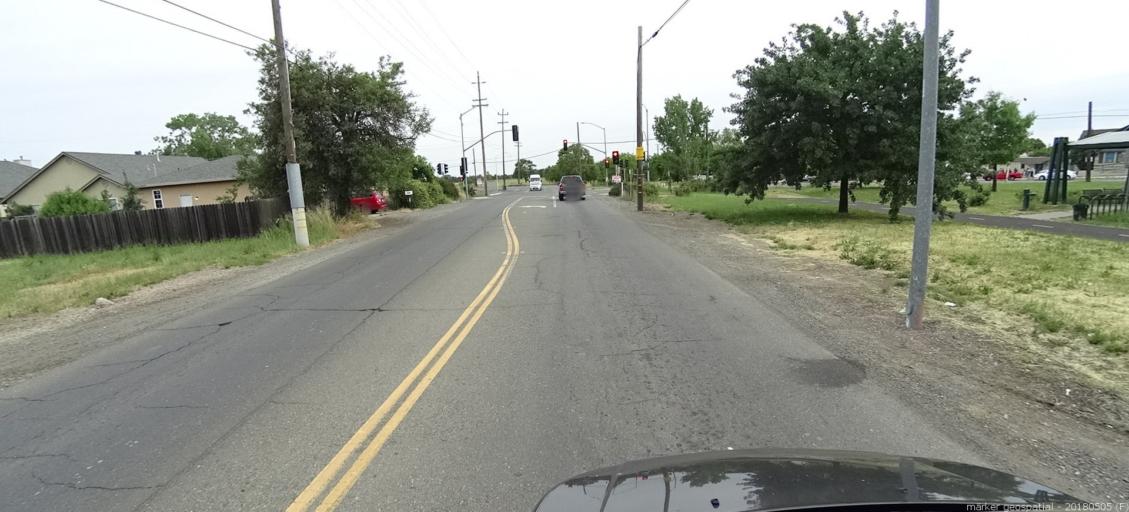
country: US
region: California
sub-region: Sacramento County
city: Rio Linda
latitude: 38.6613
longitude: -121.4477
